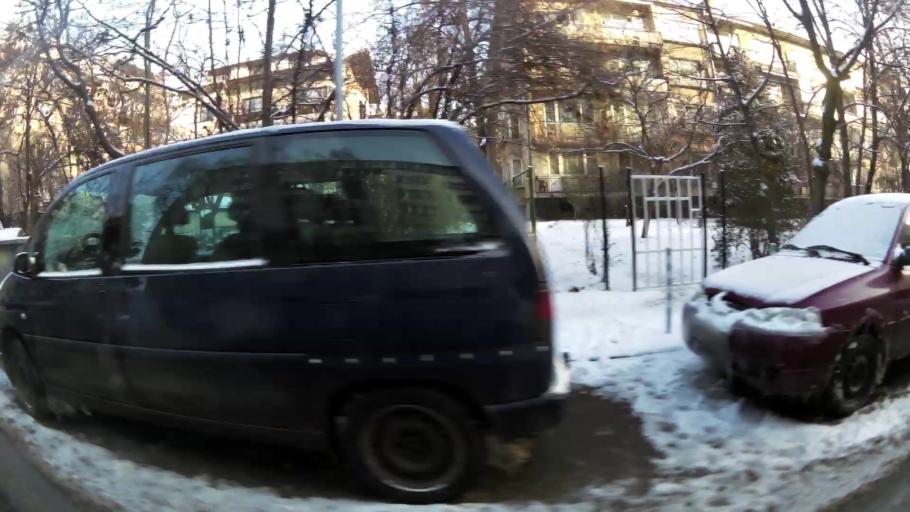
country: BG
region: Sofia-Capital
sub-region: Stolichna Obshtina
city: Sofia
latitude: 42.6705
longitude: 23.3248
